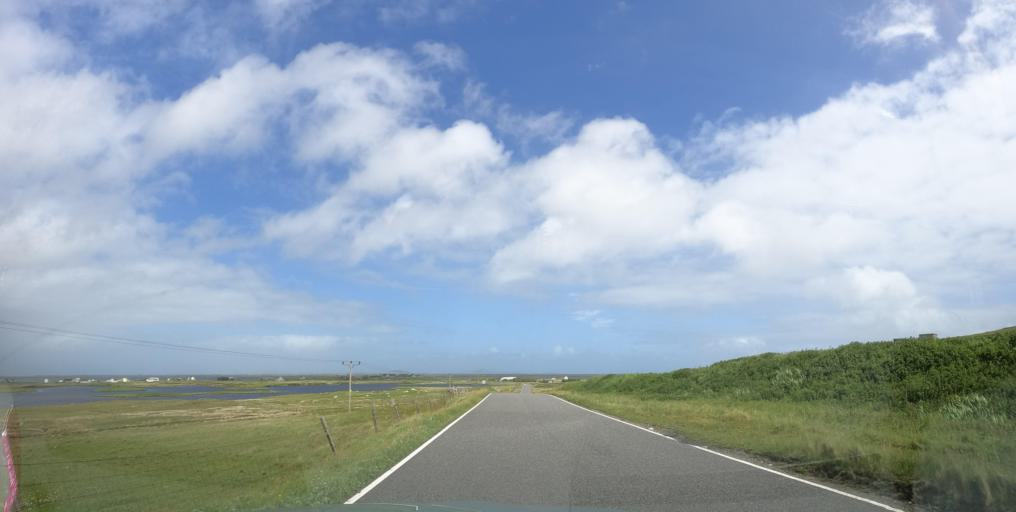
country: GB
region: Scotland
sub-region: Eilean Siar
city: Benbecula
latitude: 57.3456
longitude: -7.3628
